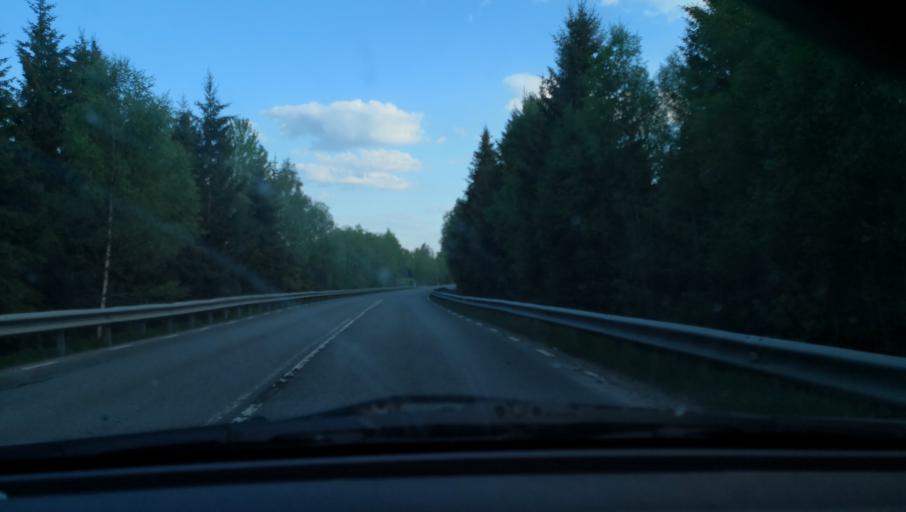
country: SE
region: Joenkoeping
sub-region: Nassjo Kommun
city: Nassjo
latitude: 57.5813
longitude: 14.6888
